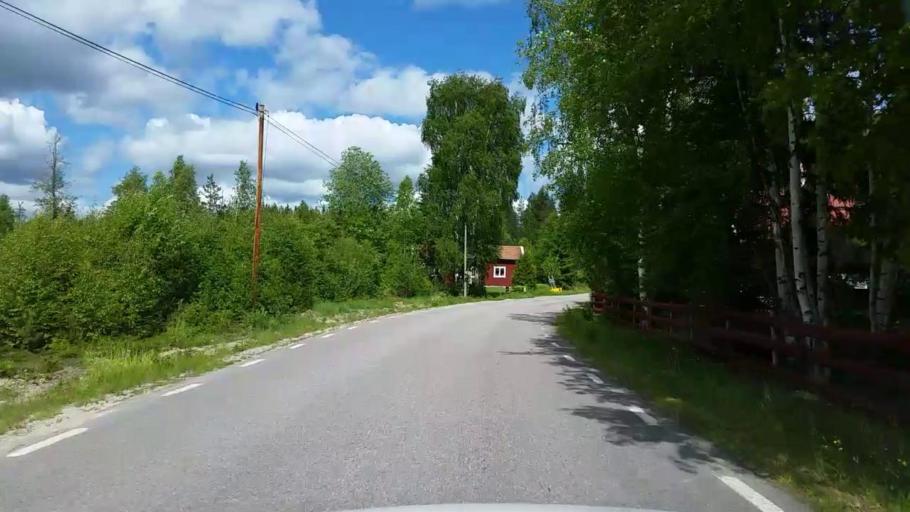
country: SE
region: Gaevleborg
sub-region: Ovanakers Kommun
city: Alfta
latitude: 61.4044
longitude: 16.0523
